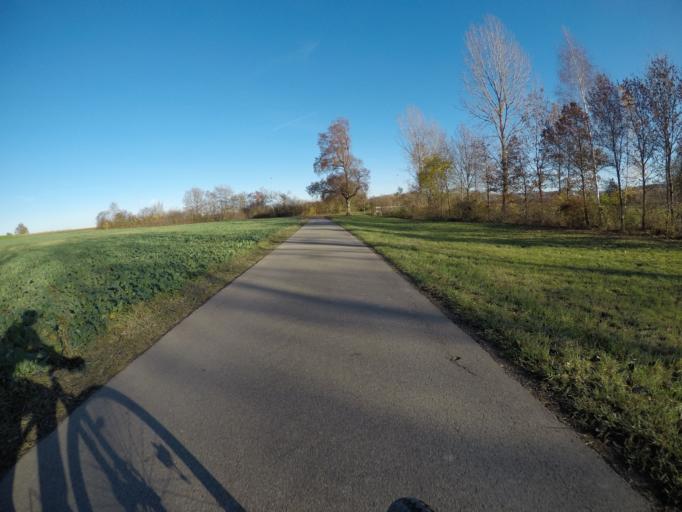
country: DE
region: Baden-Wuerttemberg
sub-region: Regierungsbezirk Stuttgart
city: Ehningen
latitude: 48.6835
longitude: 8.9637
